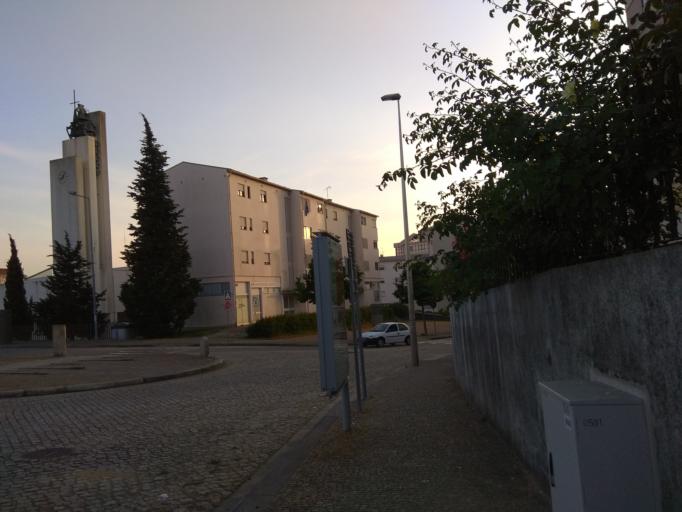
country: PT
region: Porto
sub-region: Maia
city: Maia
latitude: 41.2313
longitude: -8.6211
